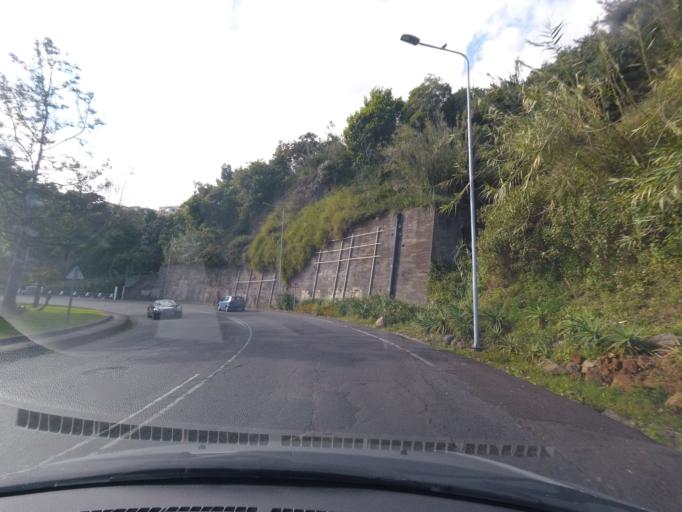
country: PT
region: Madeira
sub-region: Funchal
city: Nossa Senhora do Monte
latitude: 32.6583
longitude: -16.8835
